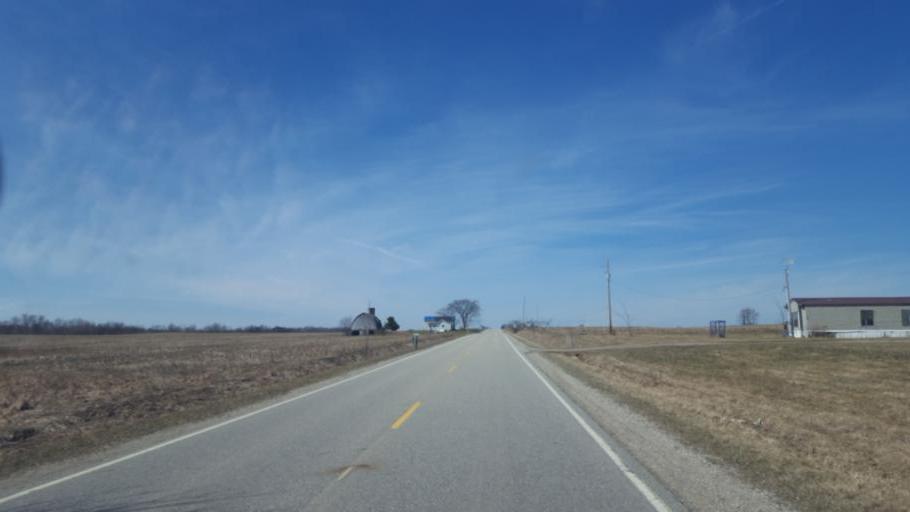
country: US
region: Michigan
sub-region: Montcalm County
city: Edmore
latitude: 43.4661
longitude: -85.0661
